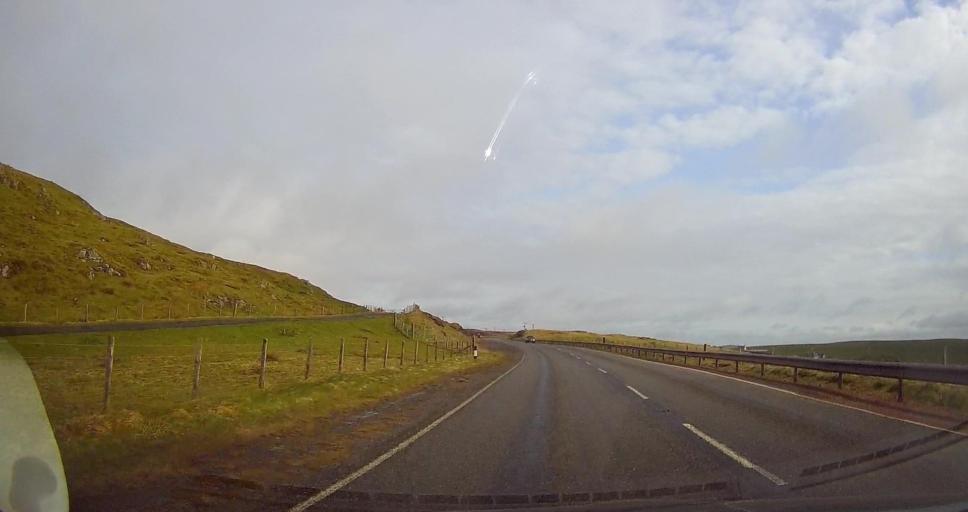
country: GB
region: Scotland
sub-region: Shetland Islands
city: Lerwick
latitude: 60.1097
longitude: -1.2194
